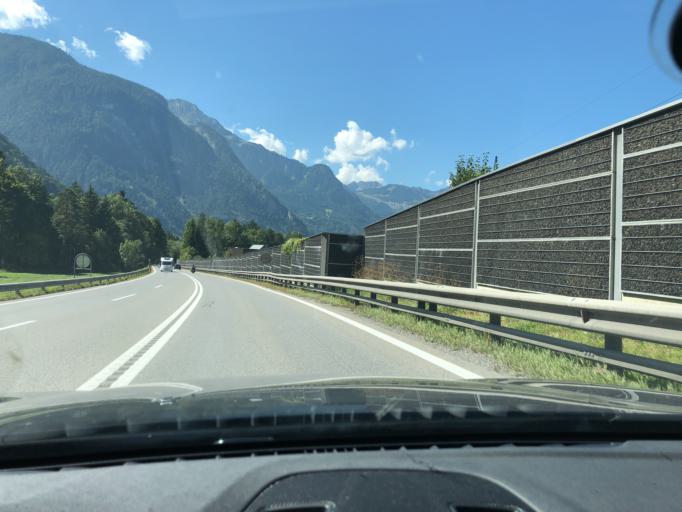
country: AT
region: Vorarlberg
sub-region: Politischer Bezirk Bludenz
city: Stallehr
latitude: 47.1440
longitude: 9.8641
